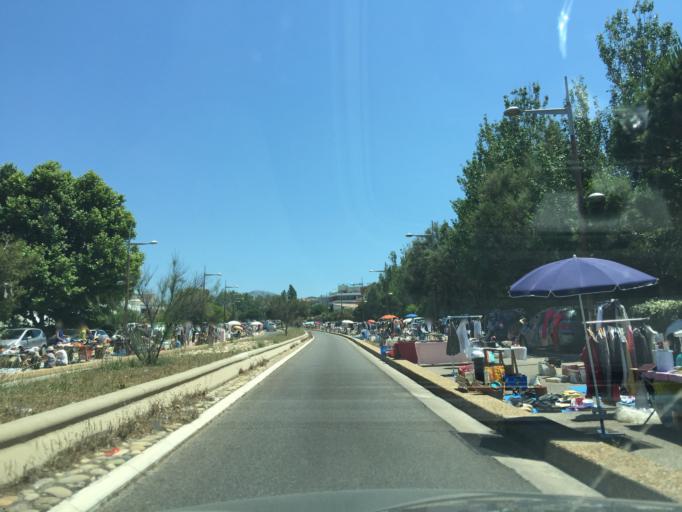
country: FR
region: Provence-Alpes-Cote d'Azur
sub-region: Departement des Bouches-du-Rhone
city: Marseille 08
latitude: 43.2451
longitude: 5.3760
